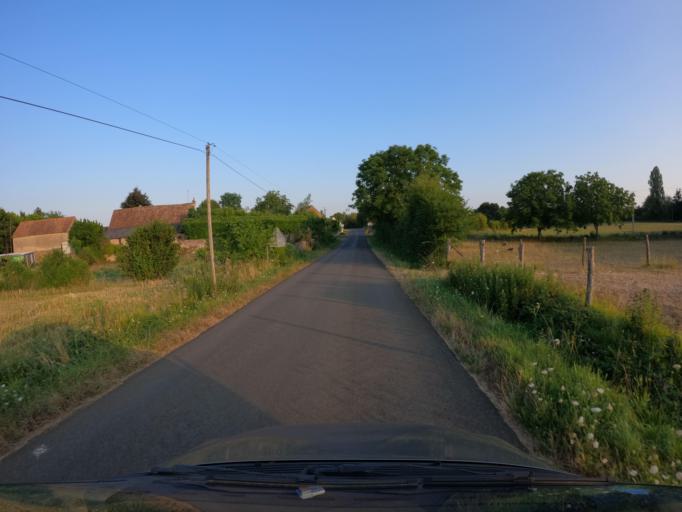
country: FR
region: Pays de la Loire
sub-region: Departement de la Sarthe
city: Brulon
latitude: 47.9069
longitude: -0.2225
